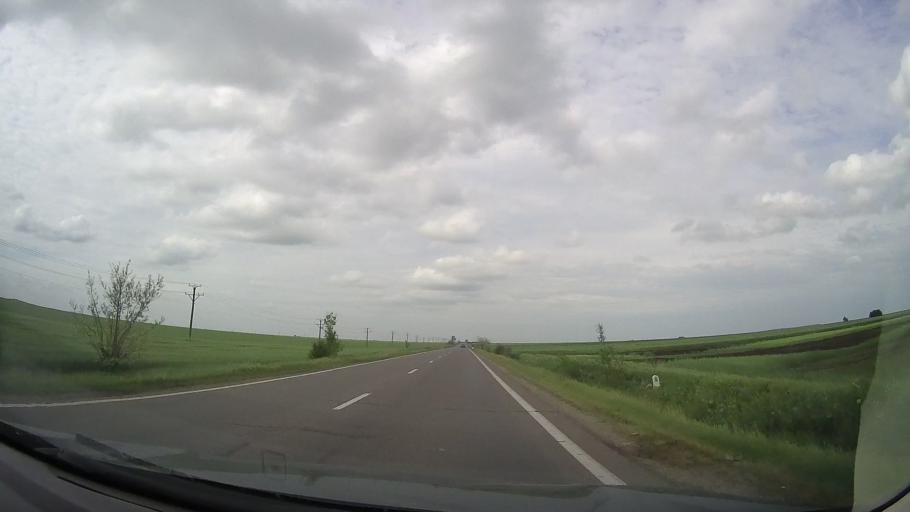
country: RO
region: Teleorman
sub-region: Comuna Draganesti-Vlasca
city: Draganesti-Vlasca
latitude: 44.0640
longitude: 25.5261
